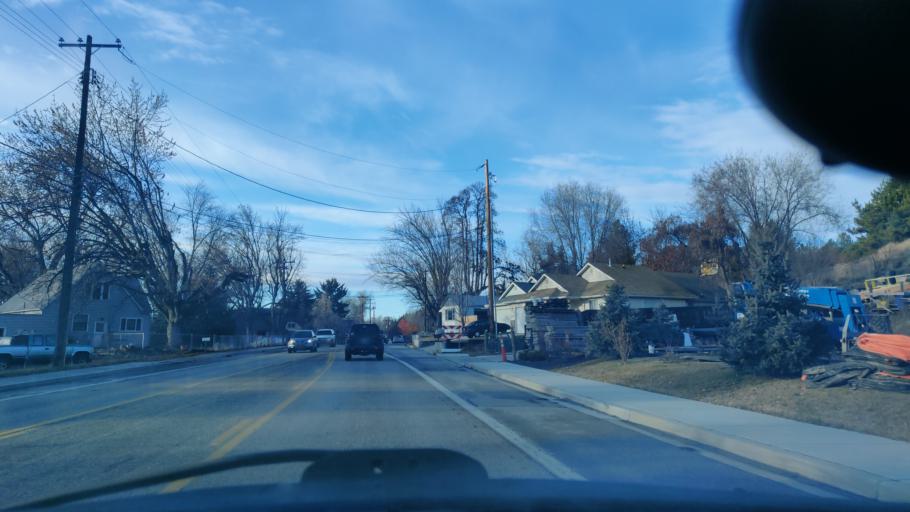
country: US
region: Idaho
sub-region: Ada County
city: Garden City
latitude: 43.6455
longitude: -116.2175
